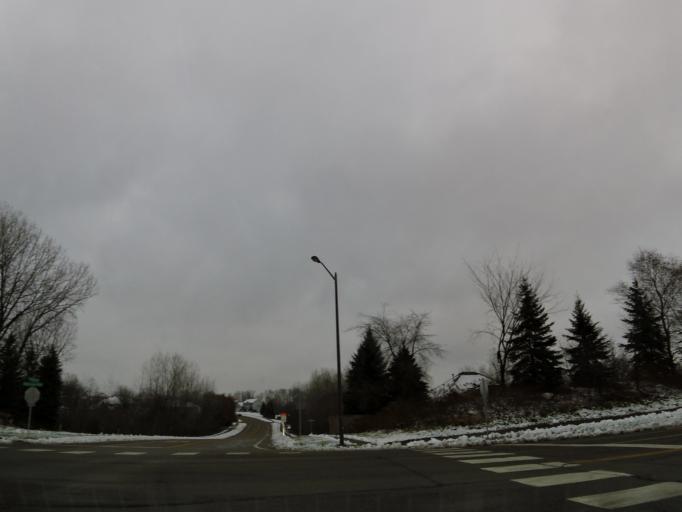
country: US
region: Minnesota
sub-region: Dakota County
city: Apple Valley
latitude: 44.7101
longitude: -93.2381
